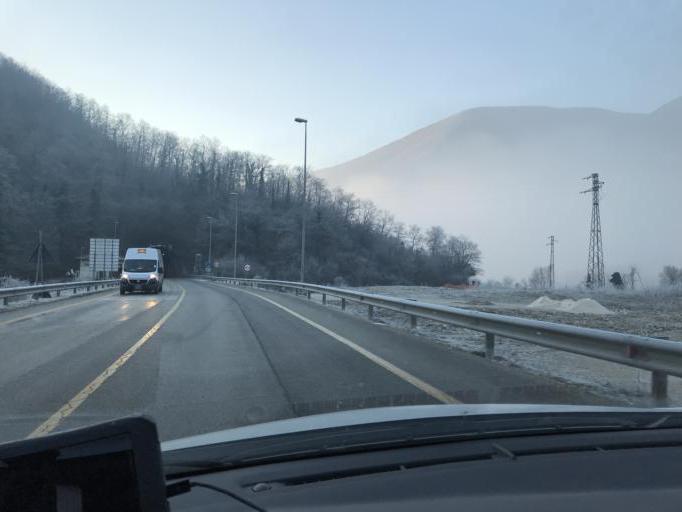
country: IT
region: Latium
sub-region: Provincia di Rieti
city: Colli sul Velino
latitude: 42.5041
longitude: 12.7467
